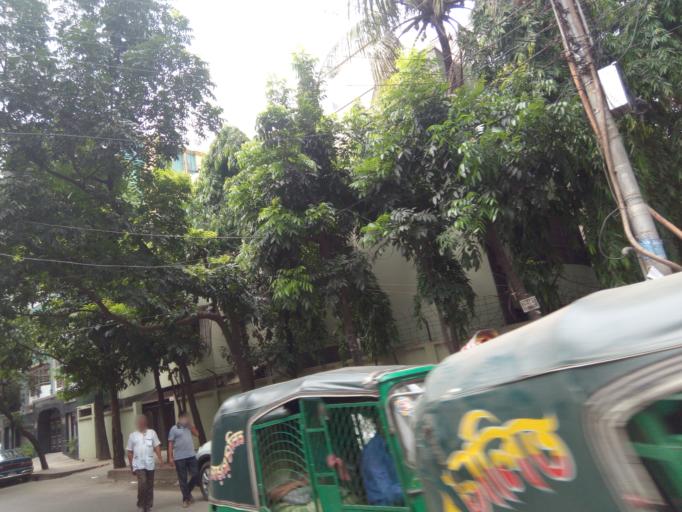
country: BD
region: Dhaka
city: Azimpur
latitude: 23.7512
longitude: 90.3708
